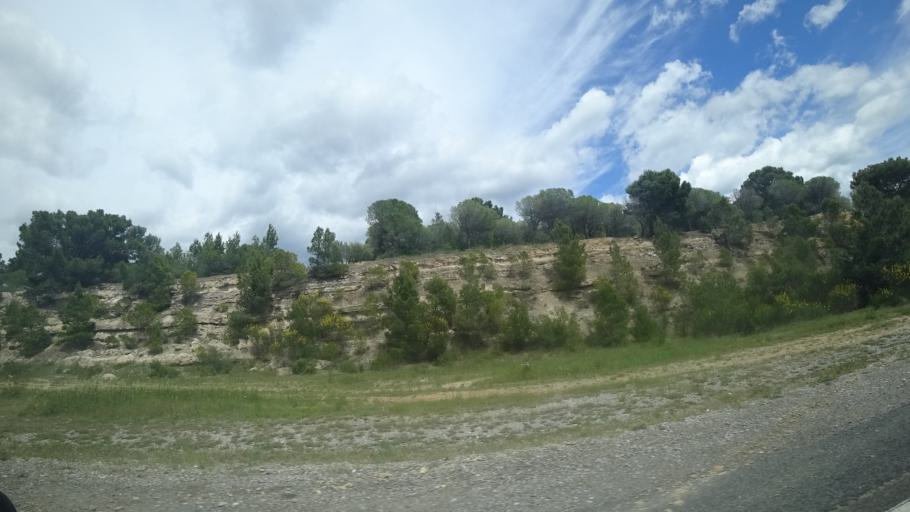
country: FR
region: Languedoc-Roussillon
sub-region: Departement de l'Aude
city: Leucate
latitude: 42.9164
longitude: 3.0213
